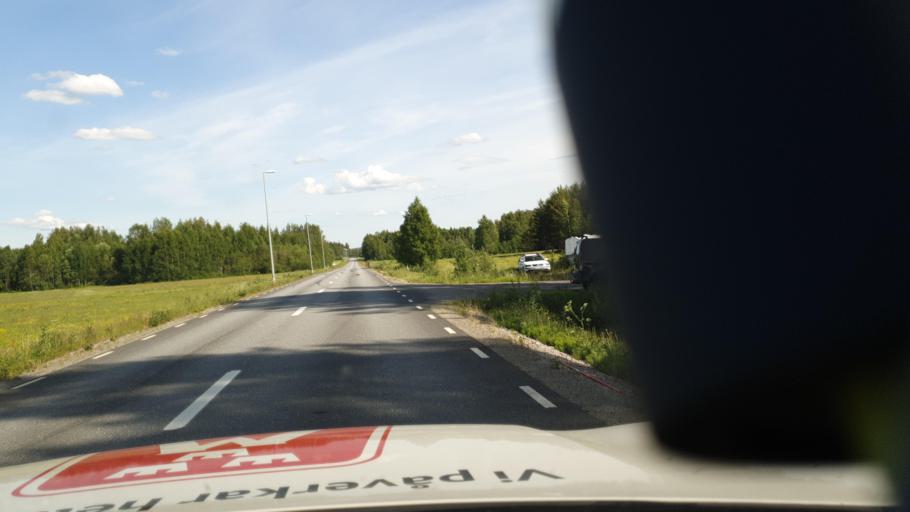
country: SE
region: Vaesterbotten
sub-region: Skelleftea Kommun
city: Forsbacka
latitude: 64.6979
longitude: 20.4769
